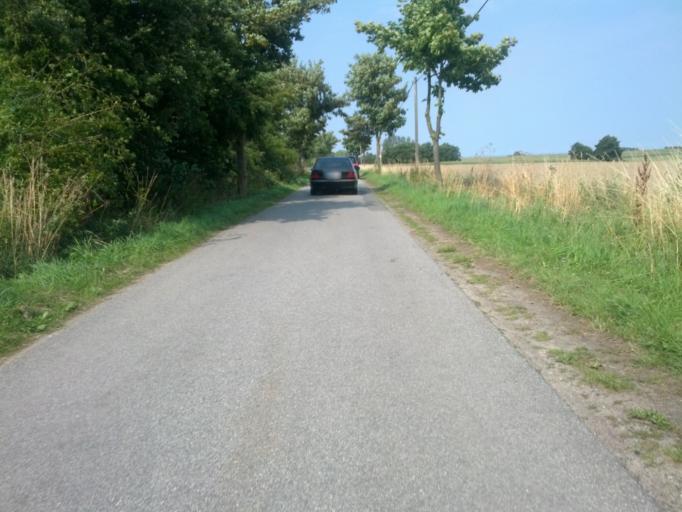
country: DE
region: Mecklenburg-Vorpommern
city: Bastorf
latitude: 54.1181
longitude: 11.6634
